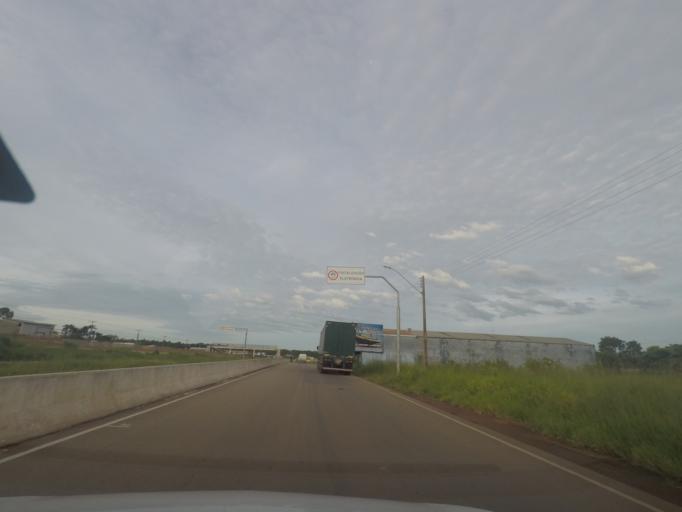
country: BR
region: Goias
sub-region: Goiania
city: Goiania
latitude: -16.7243
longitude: -49.3784
